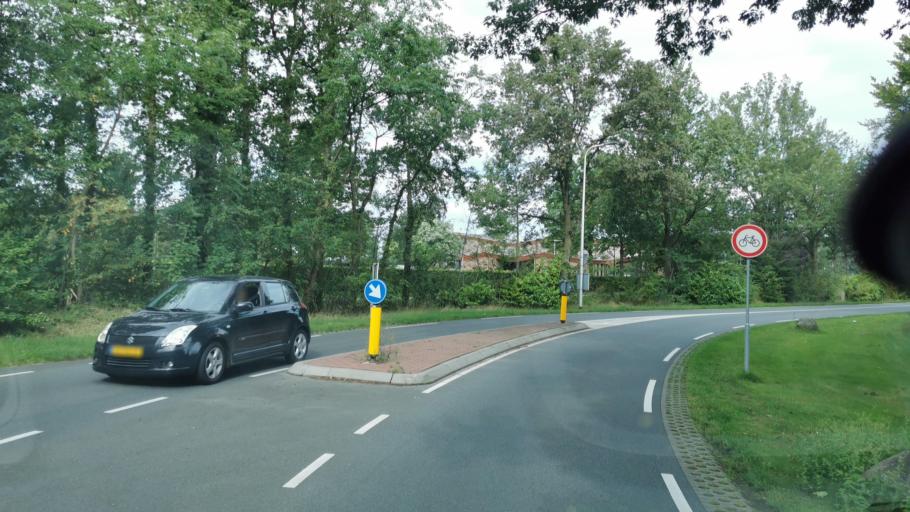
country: NL
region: Overijssel
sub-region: Gemeente Oldenzaal
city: Oldenzaal
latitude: 52.3117
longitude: 6.8943
